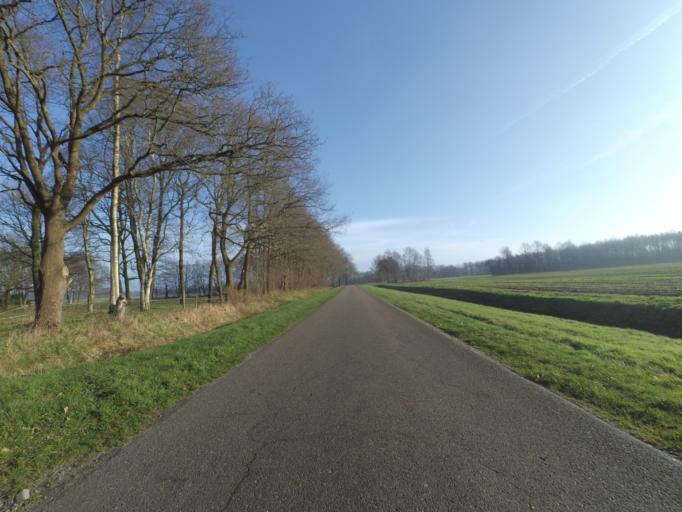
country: NL
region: Drenthe
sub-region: Gemeente Assen
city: Assen
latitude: 52.8525
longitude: 6.6414
